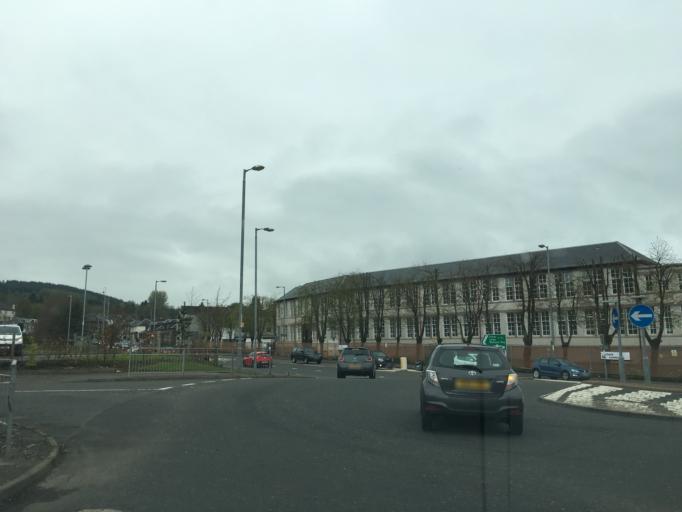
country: GB
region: Scotland
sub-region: Inverclyde
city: Greenock
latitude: 55.9415
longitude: -4.7854
